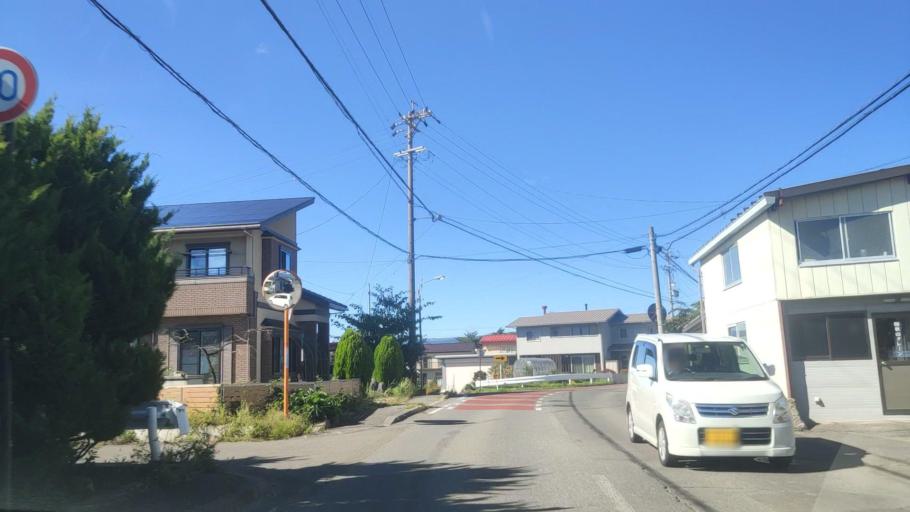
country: JP
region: Nagano
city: Chino
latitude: 35.9770
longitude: 138.2191
